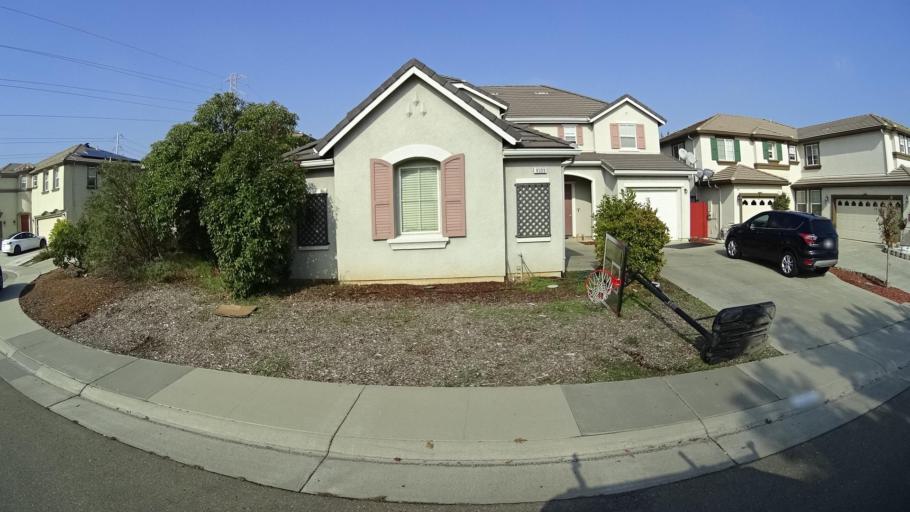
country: US
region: California
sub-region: Sacramento County
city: Elk Grove
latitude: 38.4213
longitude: -121.3503
